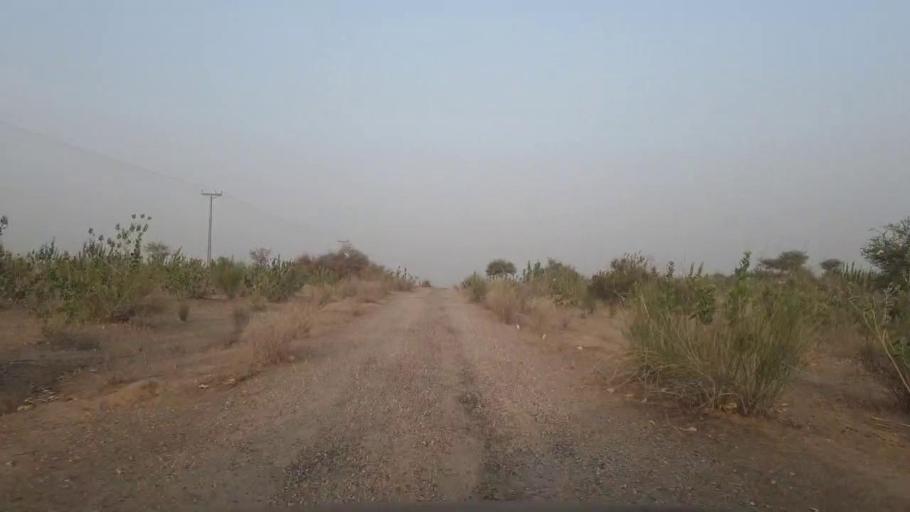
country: PK
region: Sindh
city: Chor
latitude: 25.5309
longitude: 69.9541
